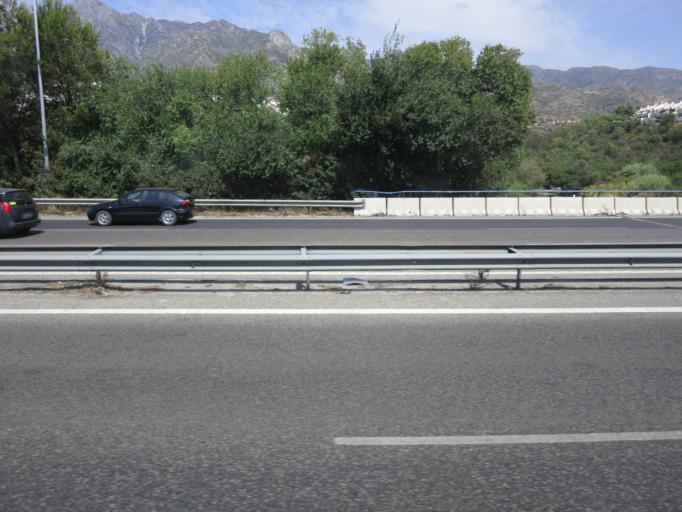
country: ES
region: Andalusia
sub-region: Provincia de Malaga
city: Marbella
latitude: 36.5164
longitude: -4.9048
